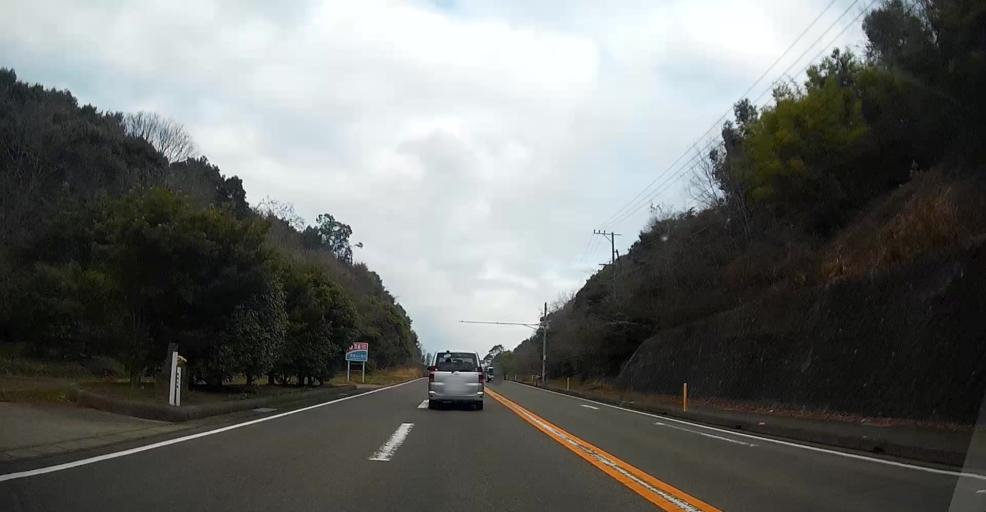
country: JP
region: Kumamoto
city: Yatsushiro
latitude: 32.5574
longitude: 130.4156
